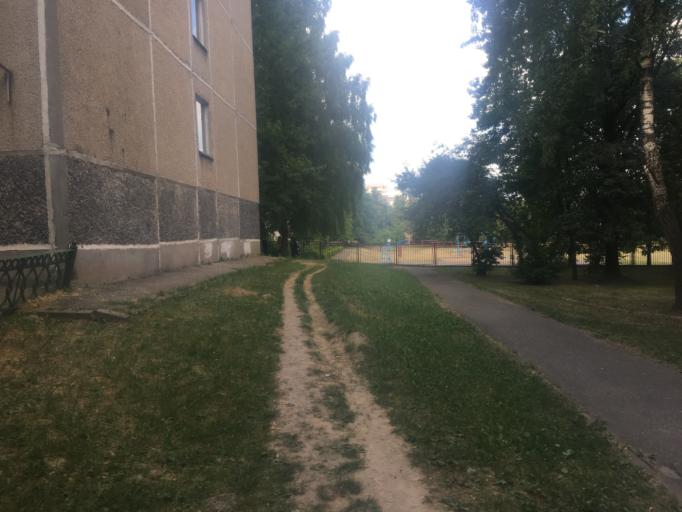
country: BY
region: Grodnenskaya
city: Hrodna
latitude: 53.7059
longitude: 23.8103
